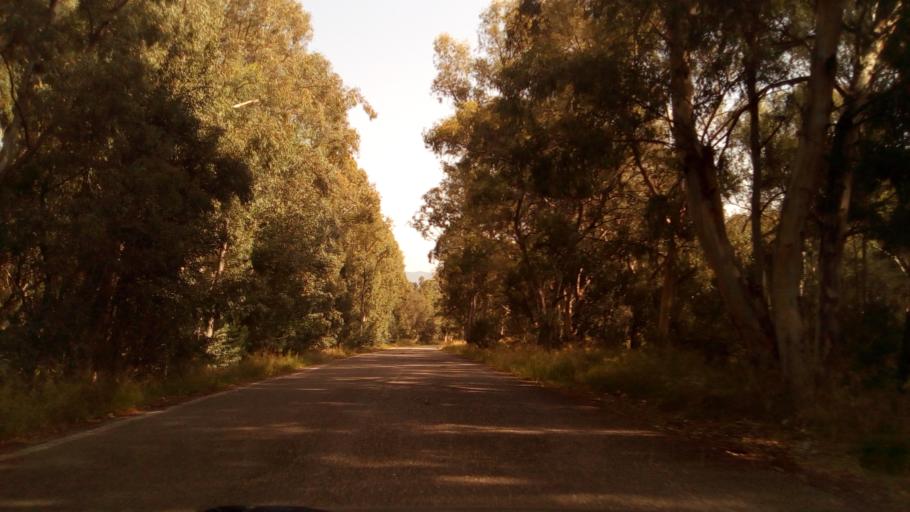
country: GR
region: West Greece
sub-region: Nomos Aitolias kai Akarnanias
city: Nafpaktos
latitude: 38.4011
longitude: 21.8734
